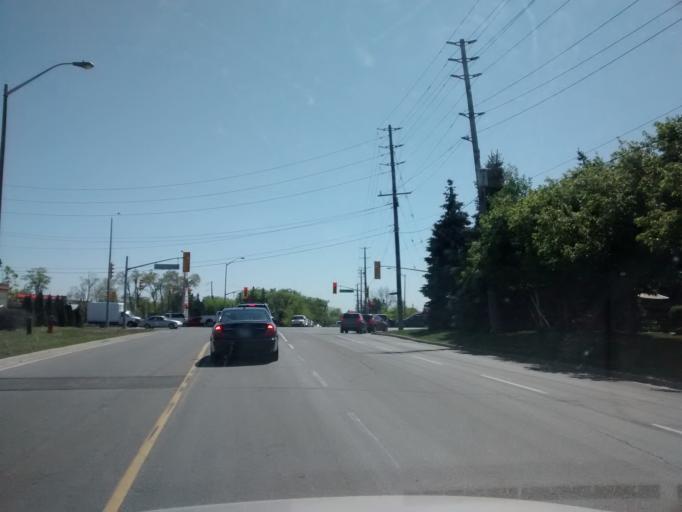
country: CA
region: Ontario
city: Burlington
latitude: 43.3564
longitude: -79.8086
